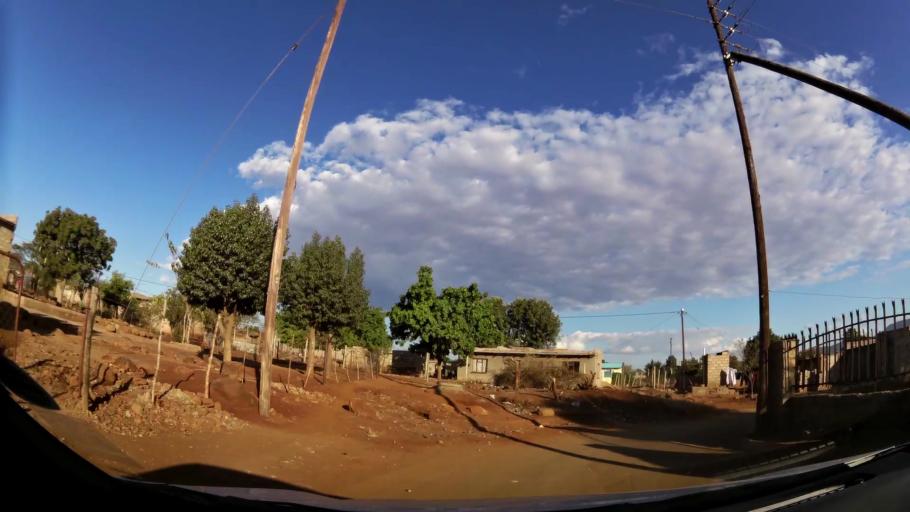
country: ZA
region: Limpopo
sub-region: Waterberg District Municipality
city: Mokopane
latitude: -24.1648
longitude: 28.9898
